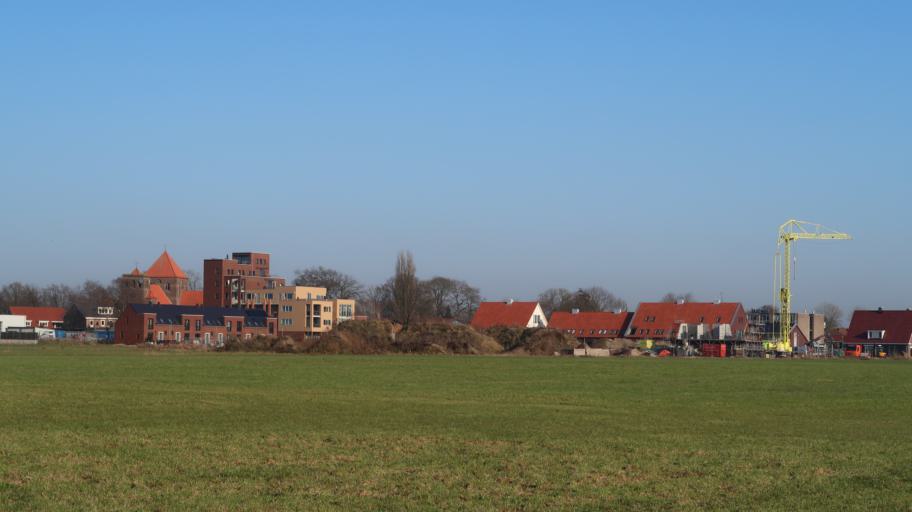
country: NL
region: Gelderland
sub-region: Gemeente Barneveld
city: Terschuur
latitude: 52.1327
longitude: 5.4893
